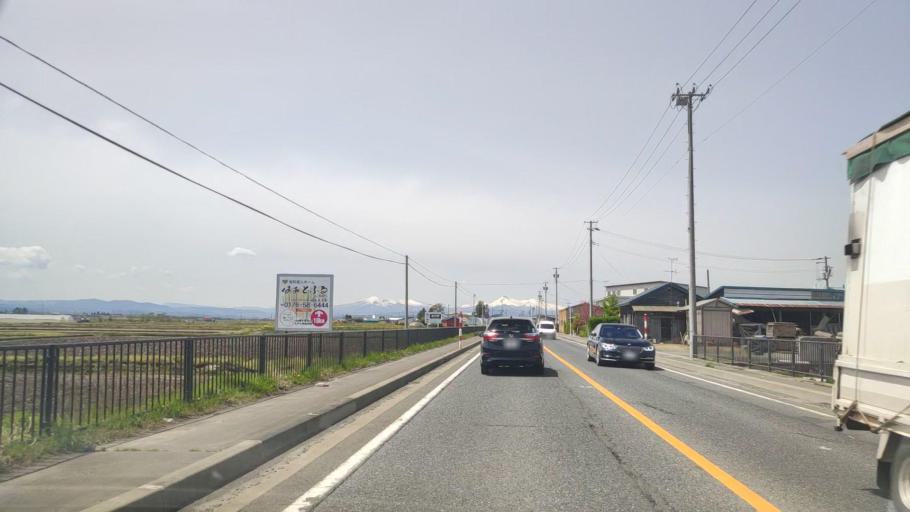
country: JP
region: Aomori
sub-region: Misawa Shi
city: Inuotose
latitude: 40.6097
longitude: 141.2818
